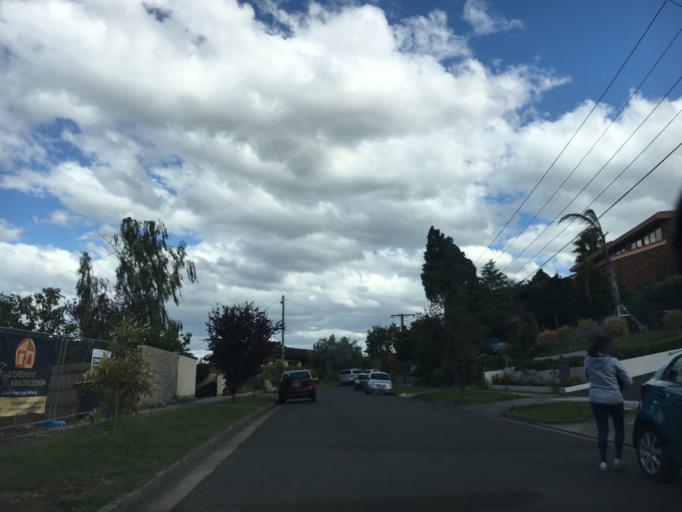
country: AU
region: Victoria
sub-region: Whitehorse
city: Vermont South
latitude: -37.8854
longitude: 145.1754
